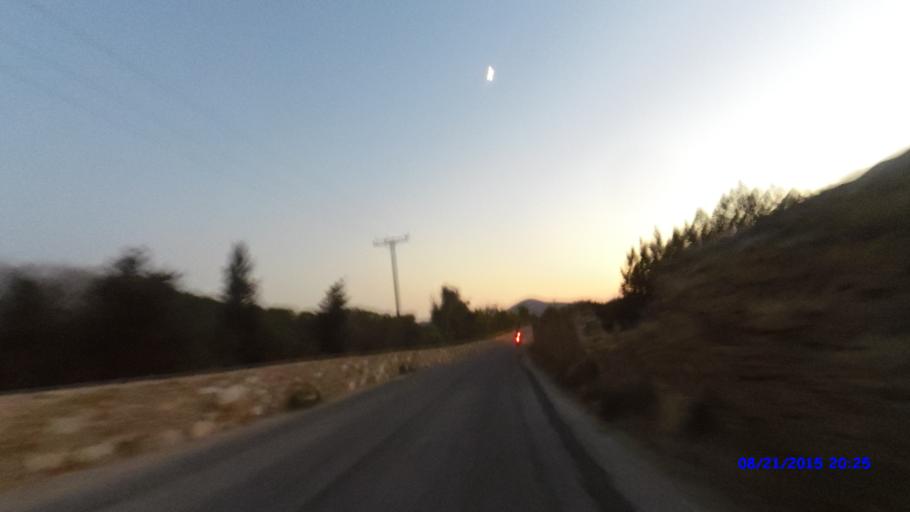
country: GR
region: South Aegean
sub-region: Nomos Kykladon
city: Antiparos
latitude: 36.9864
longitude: 25.0720
